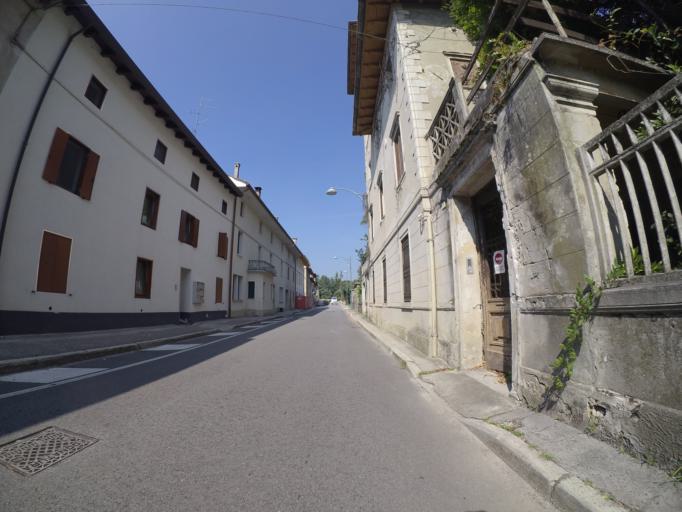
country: IT
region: Friuli Venezia Giulia
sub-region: Provincia di Udine
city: Codroipo
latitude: 45.9615
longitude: 12.9827
